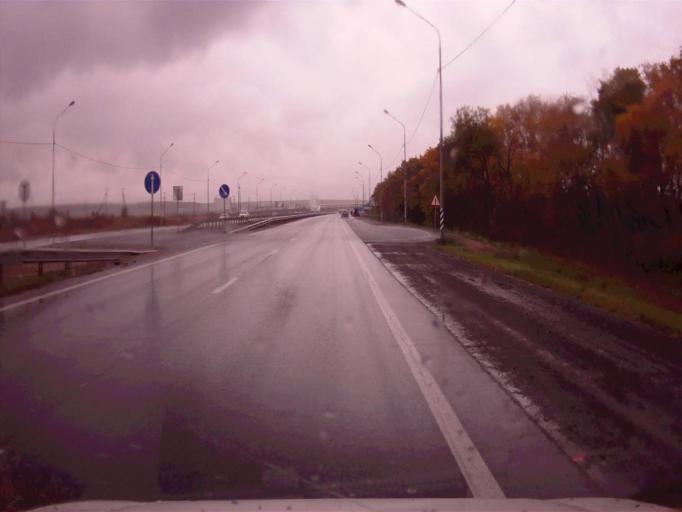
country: RU
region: Chelyabinsk
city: Dolgoderevenskoye
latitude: 55.3060
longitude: 61.3357
